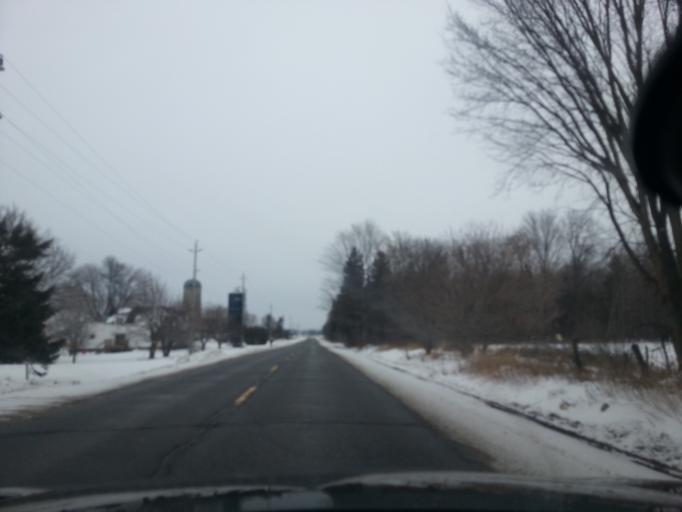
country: CA
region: Ontario
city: Arnprior
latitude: 45.3800
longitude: -76.2079
